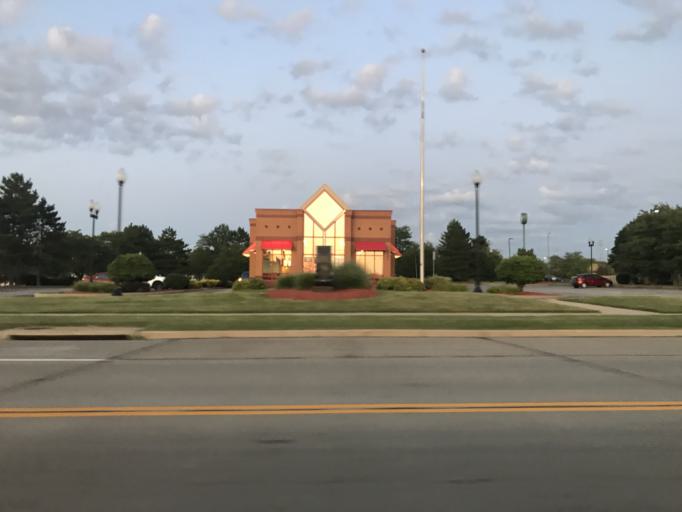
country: US
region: Ohio
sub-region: Cuyahoga County
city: Middleburg Heights
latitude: 41.3734
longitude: -81.8248
